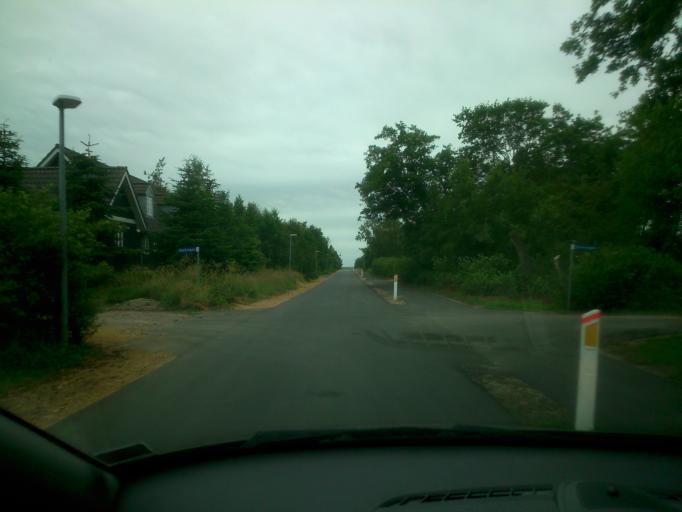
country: DK
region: Central Jutland
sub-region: Ringkobing-Skjern Kommune
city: Skjern
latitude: 55.9585
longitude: 8.3779
